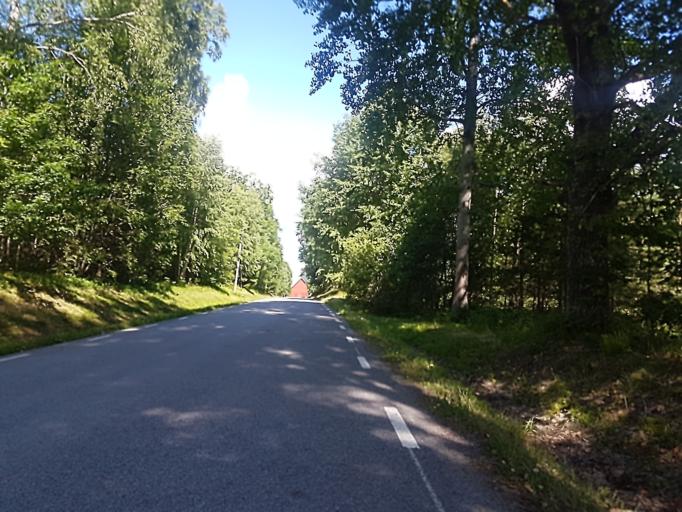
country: SE
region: Soedermanland
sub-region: Gnesta Kommun
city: Gnesta
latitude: 59.0608
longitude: 17.3354
